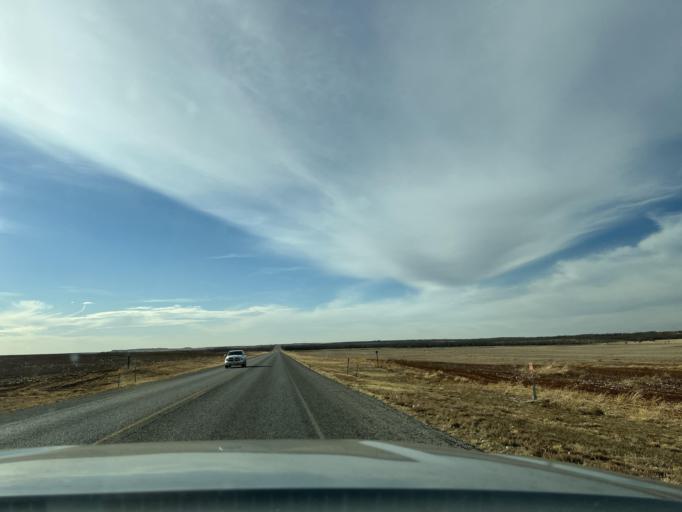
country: US
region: Texas
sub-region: Fisher County
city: Rotan
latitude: 32.7402
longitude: -100.5008
